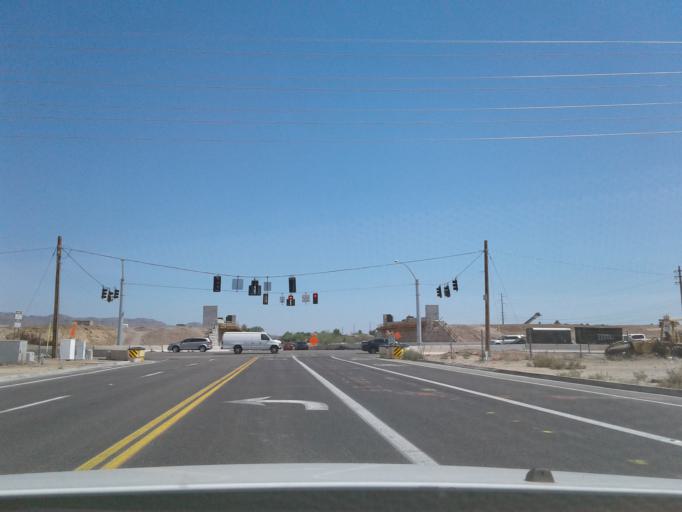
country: US
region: Arizona
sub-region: Maricopa County
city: Guadalupe
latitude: 33.2905
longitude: -111.9973
